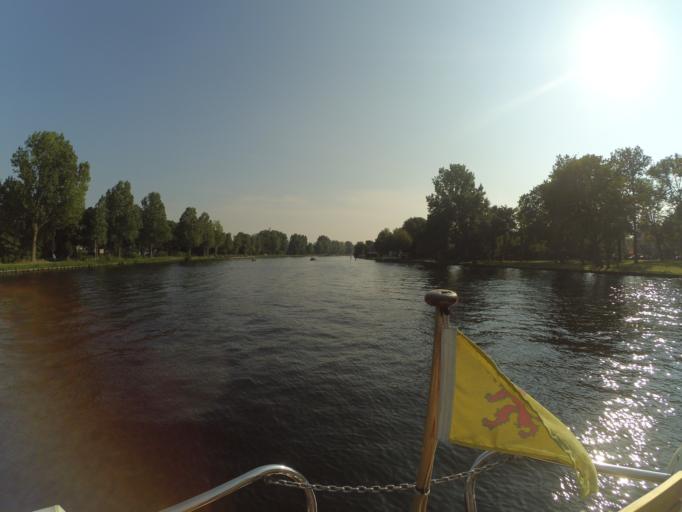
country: NL
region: North Holland
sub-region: Gemeente Haarlem
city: Haarlem
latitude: 52.3678
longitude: 4.6348
